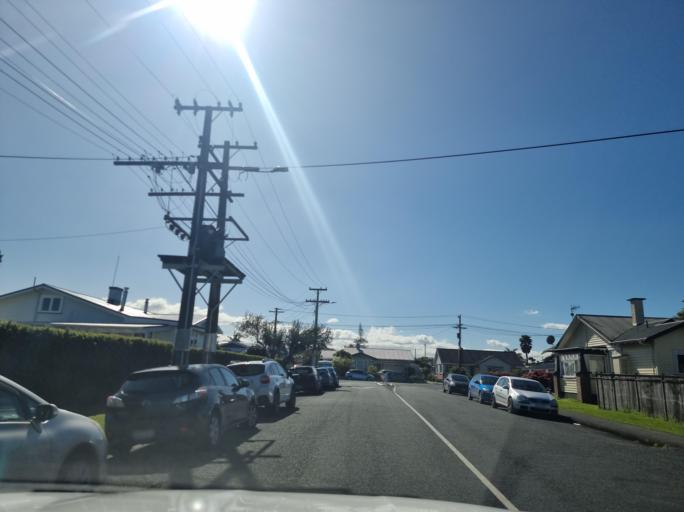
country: NZ
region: Northland
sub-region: Whangarei
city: Whangarei
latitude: -35.7128
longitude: 174.3206
